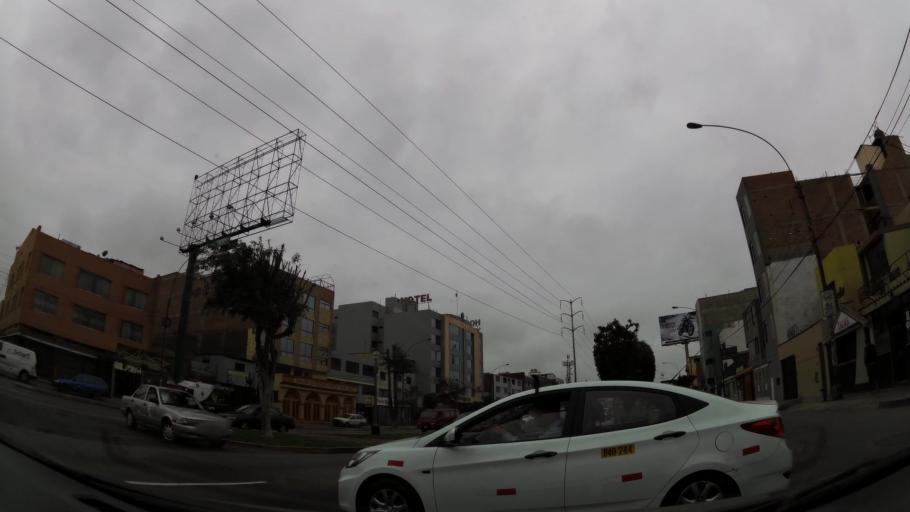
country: PE
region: Callao
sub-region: Callao
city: Callao
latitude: -12.0592
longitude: -77.0976
